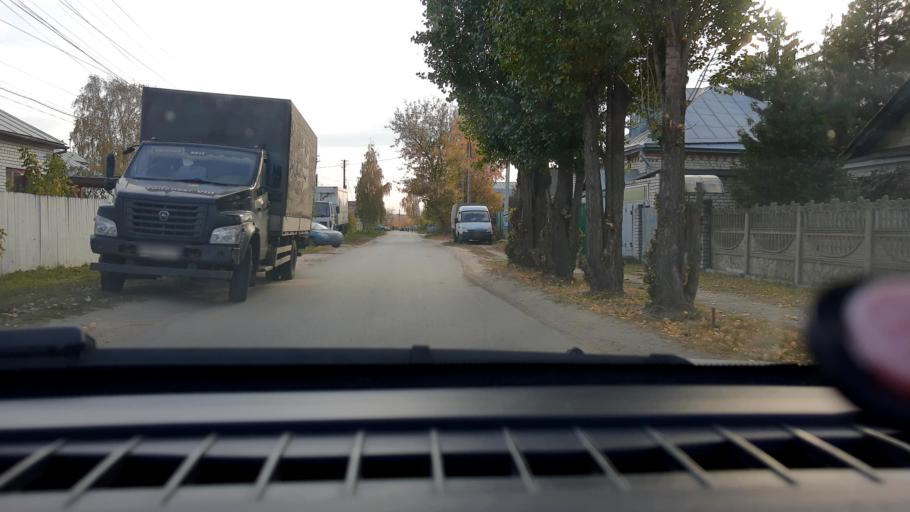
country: RU
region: Nizjnij Novgorod
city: Nizhniy Novgorod
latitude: 56.2838
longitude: 43.8995
